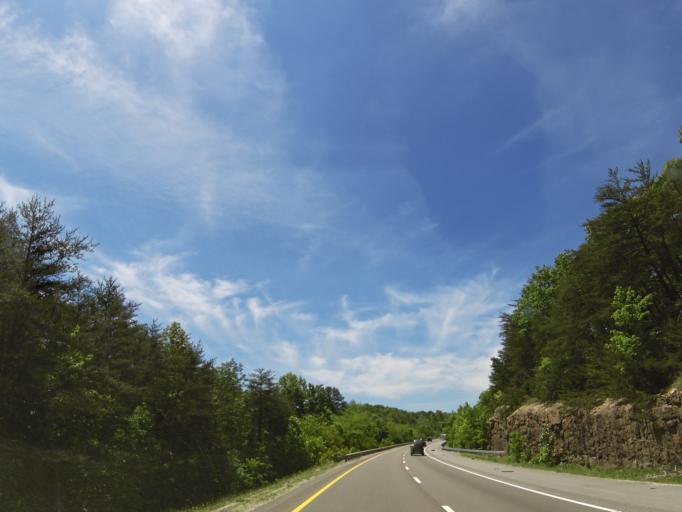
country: US
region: Tennessee
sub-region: Campbell County
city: LaFollette
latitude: 36.4756
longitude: -84.2252
